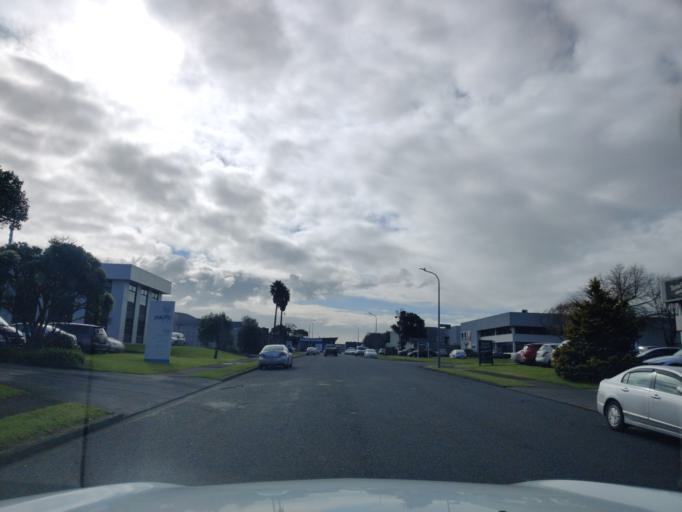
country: NZ
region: Auckland
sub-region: Auckland
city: Manukau City
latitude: -36.9395
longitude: 174.8819
